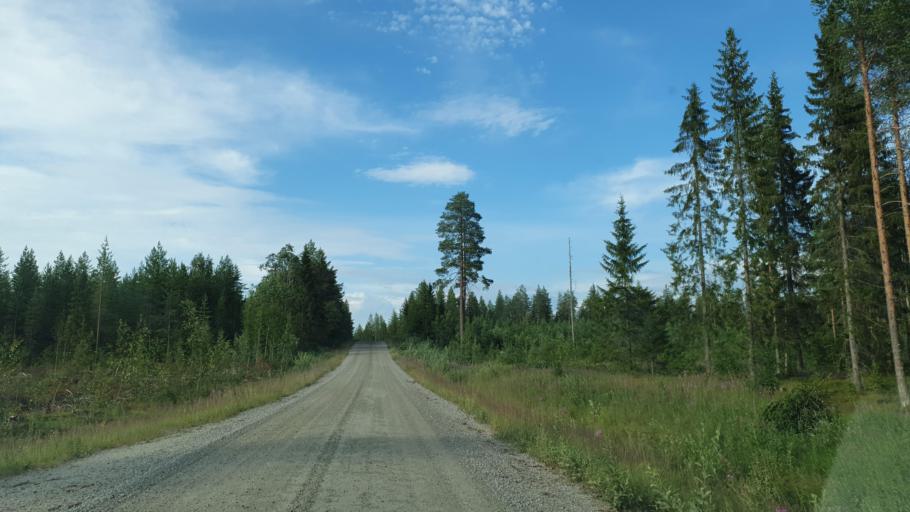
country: FI
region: Kainuu
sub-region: Kehys-Kainuu
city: Kuhmo
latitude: 64.2574
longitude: 29.4783
